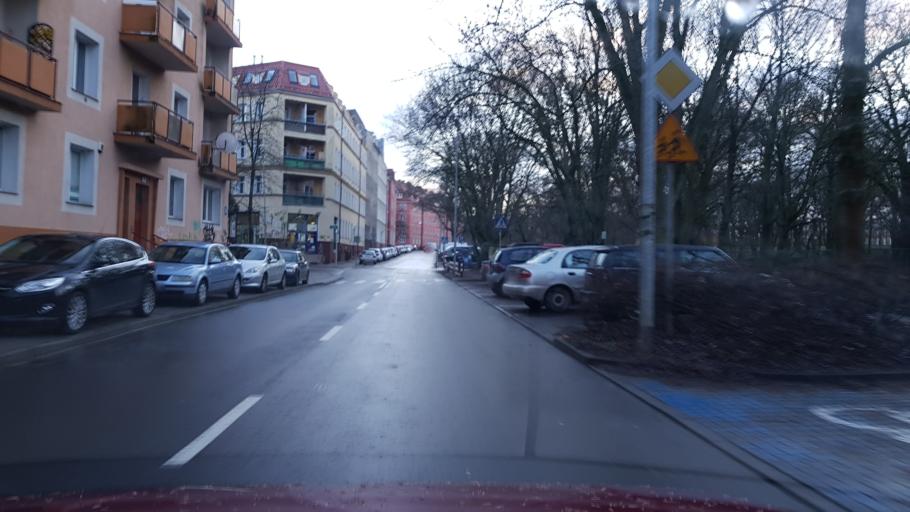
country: PL
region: West Pomeranian Voivodeship
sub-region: Szczecin
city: Szczecin
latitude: 53.4374
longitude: 14.5270
